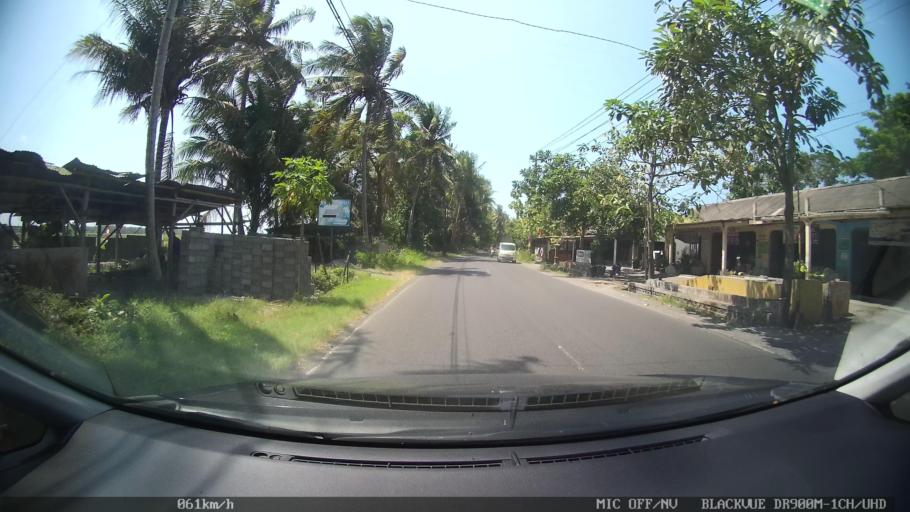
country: ID
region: Daerah Istimewa Yogyakarta
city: Srandakan
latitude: -7.9186
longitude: 110.1082
